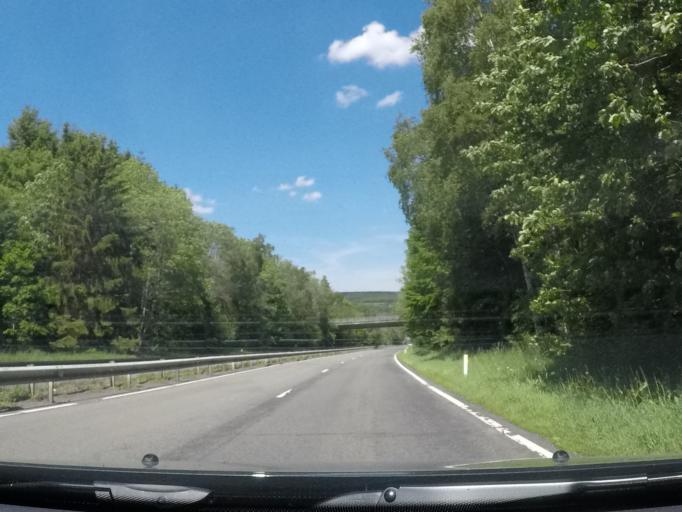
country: BE
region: Wallonia
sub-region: Province du Luxembourg
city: Saint-Hubert
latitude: 50.0213
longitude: 5.3816
